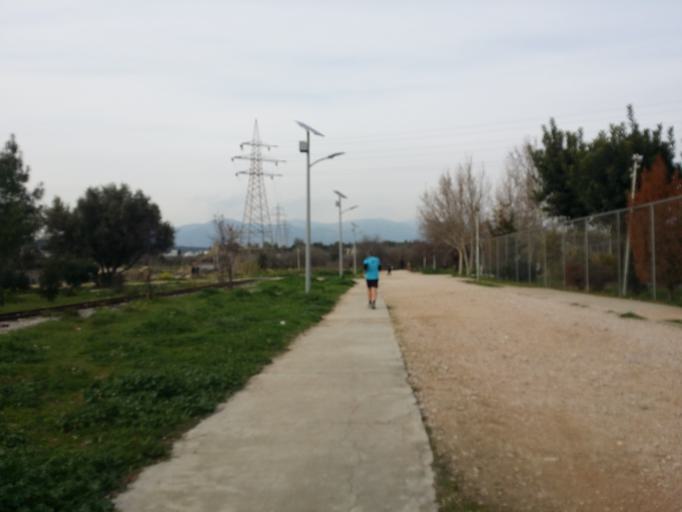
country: GR
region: Attica
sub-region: Nomarchia Athinas
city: Agioi Anargyroi
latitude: 38.0379
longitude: 23.7182
